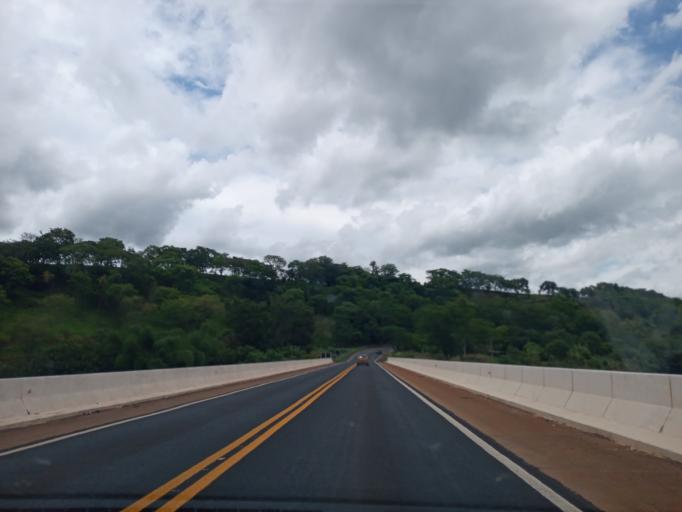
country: BR
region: Minas Gerais
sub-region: Monte Carmelo
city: Monte Carmelo
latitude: -19.2670
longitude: -47.6420
